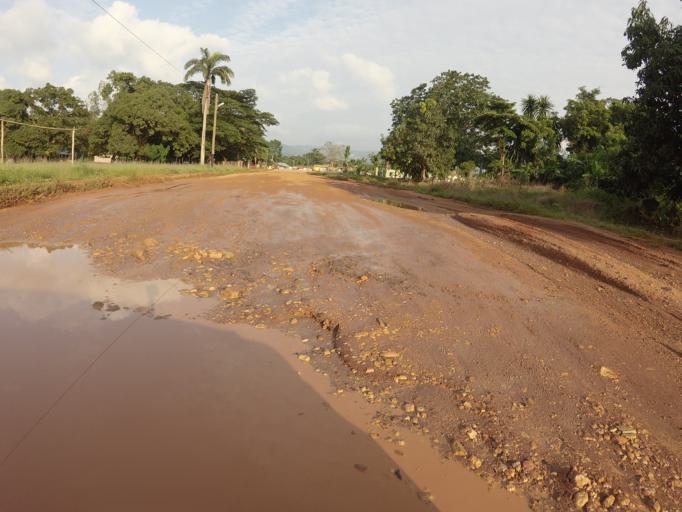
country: GH
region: Volta
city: Kpandu
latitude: 6.9648
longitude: 0.4578
